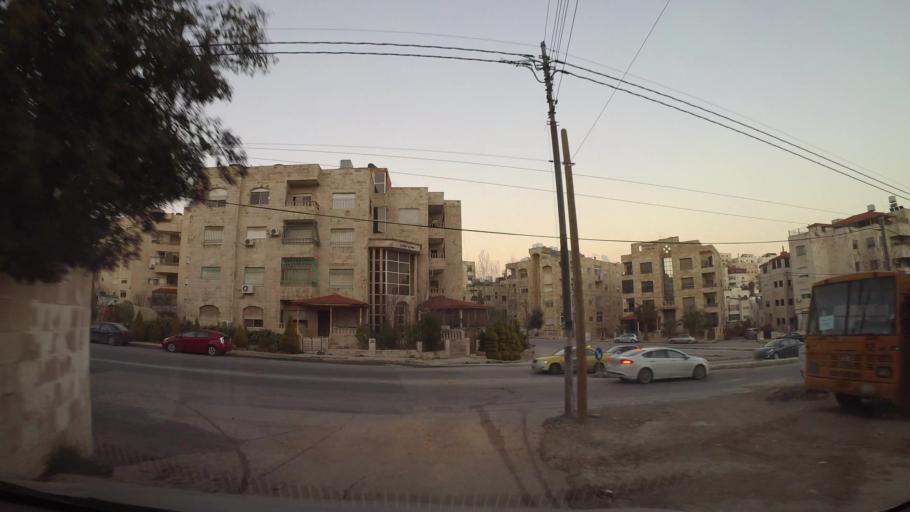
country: JO
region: Amman
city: Al Jubayhah
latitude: 31.9976
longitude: 35.8589
